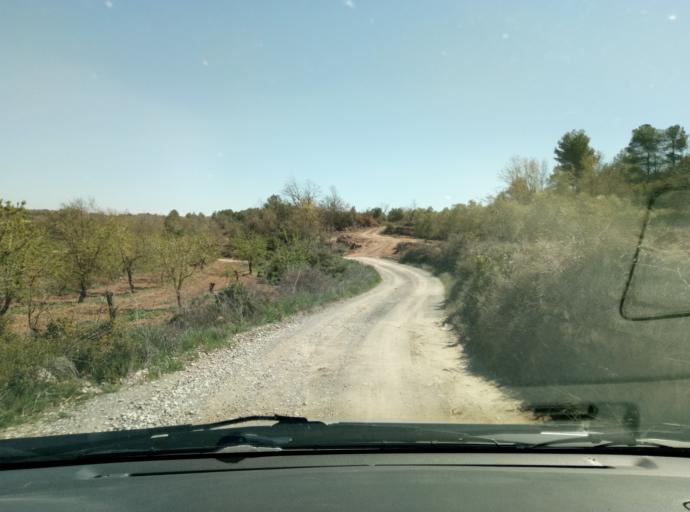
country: ES
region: Catalonia
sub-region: Provincia de Lleida
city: Vinaixa
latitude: 41.4157
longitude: 0.9167
